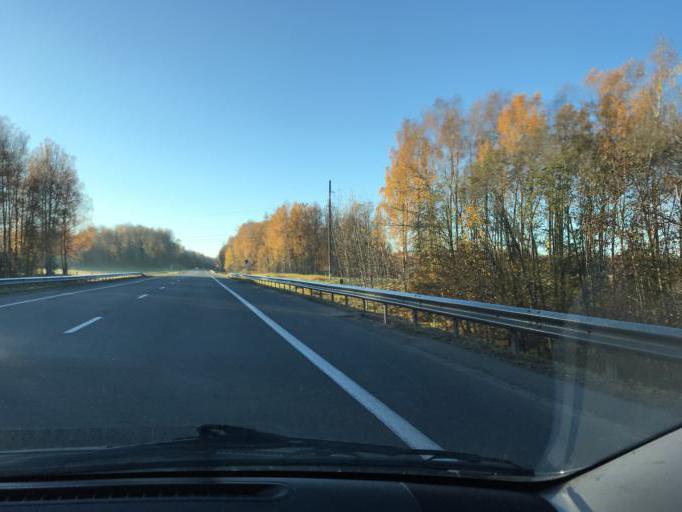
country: BY
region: Vitebsk
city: Vitebsk
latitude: 55.0417
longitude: 30.3164
